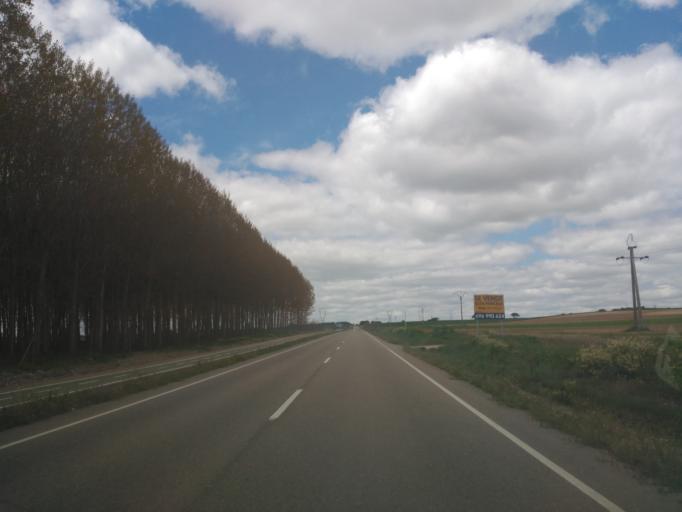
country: ES
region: Castille and Leon
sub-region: Provincia de Salamanca
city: Villamayor
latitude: 41.0253
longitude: -5.7241
